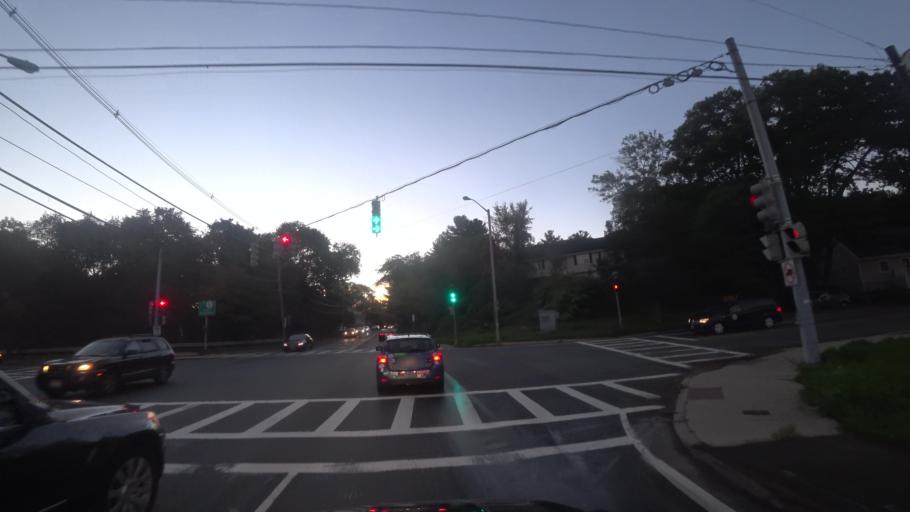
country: US
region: Massachusetts
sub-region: Essex County
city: Saugus
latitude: 42.4724
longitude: -71.0358
